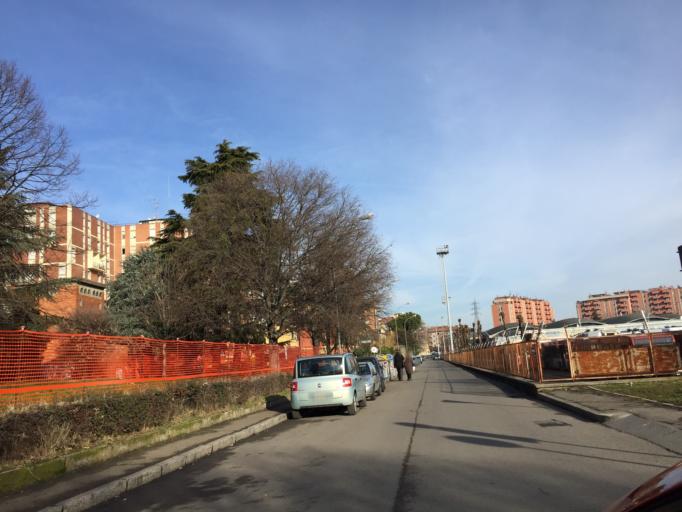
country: IT
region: Emilia-Romagna
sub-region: Provincia di Bologna
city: Casalecchio di Reno
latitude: 44.5005
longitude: 11.2945
